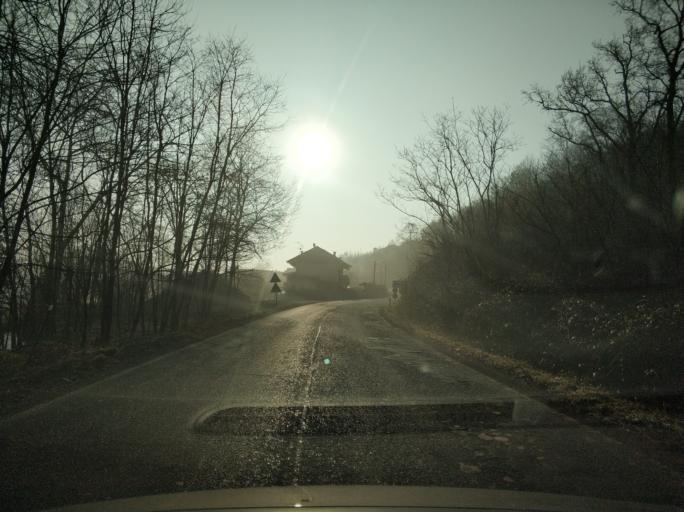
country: IT
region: Piedmont
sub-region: Provincia di Torino
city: Rivarossa
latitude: 45.2546
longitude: 7.7099
